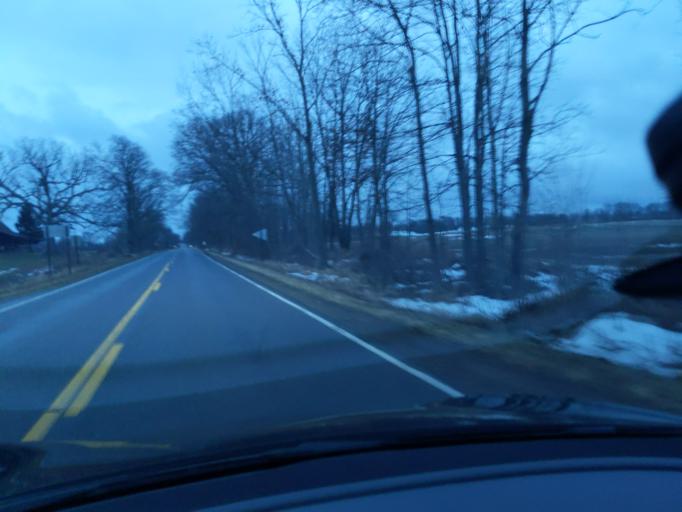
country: US
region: Michigan
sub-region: Eaton County
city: Eaton Rapids
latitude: 42.4368
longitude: -84.5605
